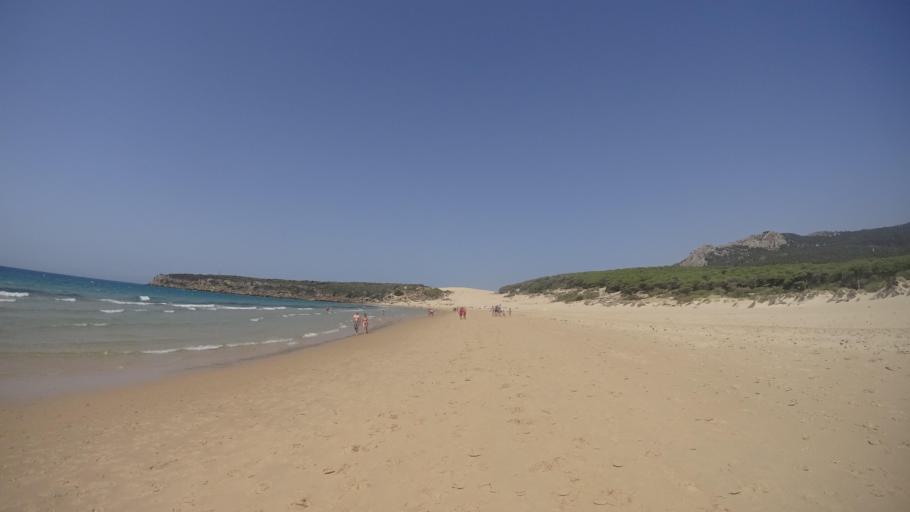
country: ES
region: Andalusia
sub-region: Provincia de Cadiz
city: Zahara de los Atunes
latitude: 36.0882
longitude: -5.7771
